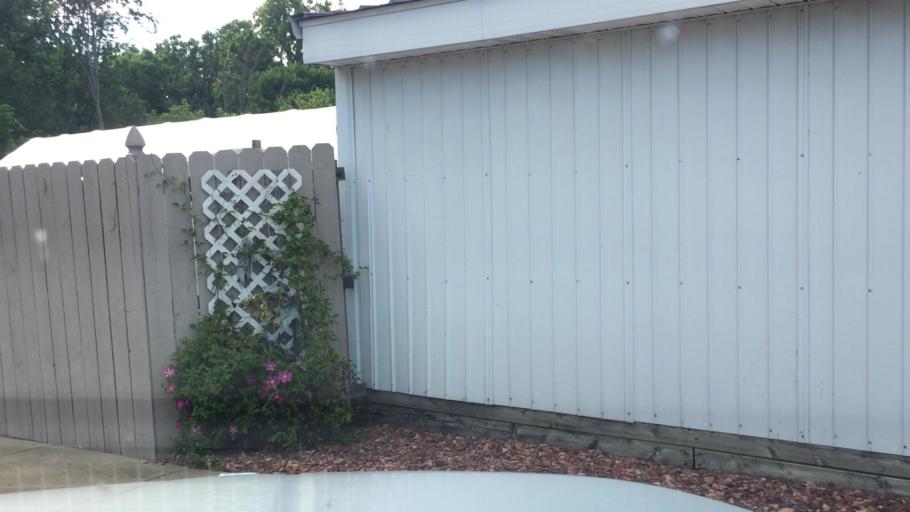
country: US
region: Michigan
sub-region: Saint Clair County
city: Yale
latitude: 43.1314
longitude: -82.7989
